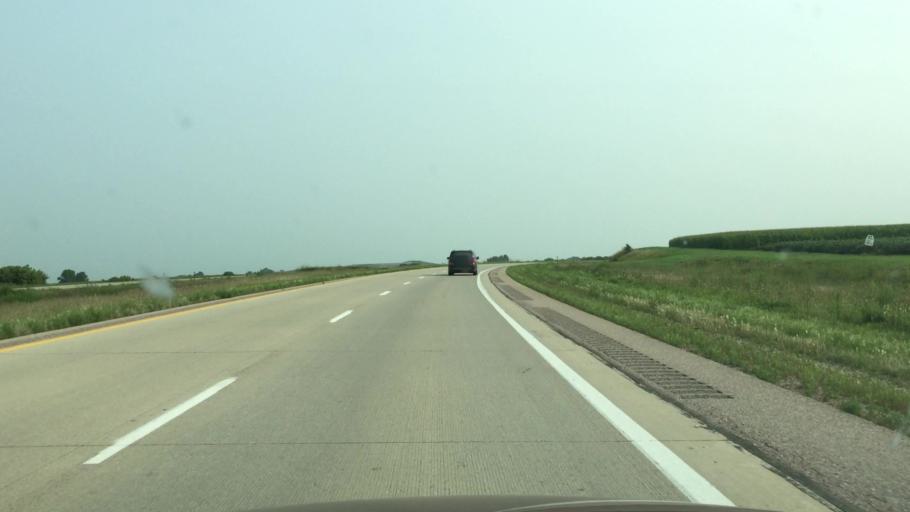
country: US
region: Iowa
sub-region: O'Brien County
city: Sheldon
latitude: 43.1083
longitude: -95.8980
